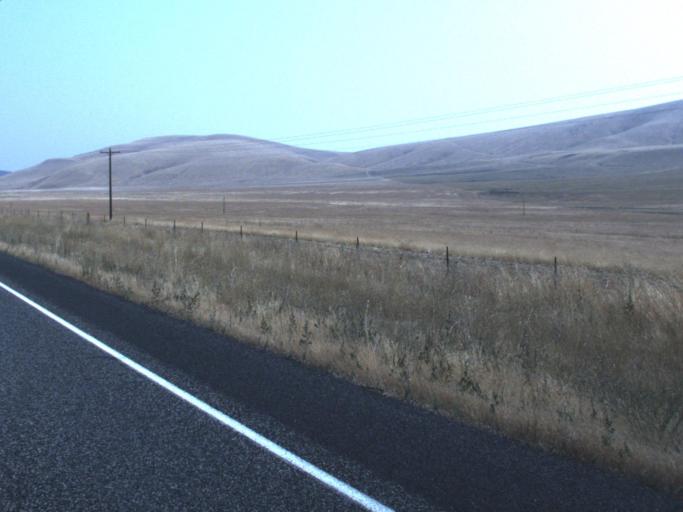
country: US
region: Washington
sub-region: Grant County
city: Desert Aire
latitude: 46.5214
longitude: -119.9627
